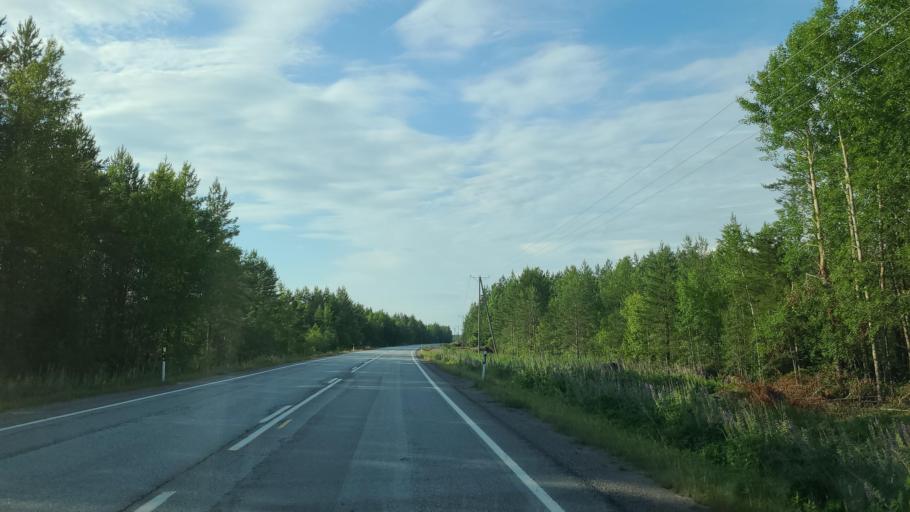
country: FI
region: Ostrobothnia
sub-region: Vaasa
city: Vaasa
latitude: 63.1577
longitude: 21.5939
